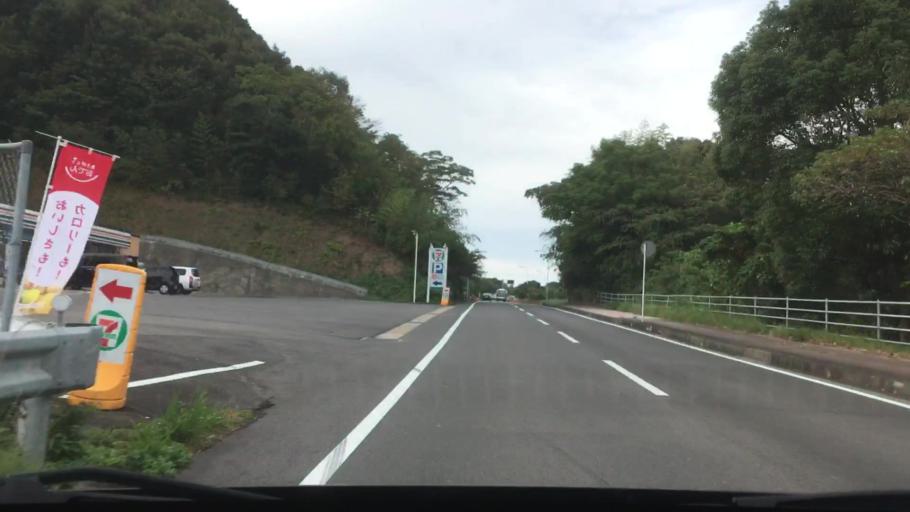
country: JP
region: Nagasaki
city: Sasebo
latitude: 33.0397
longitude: 129.6505
